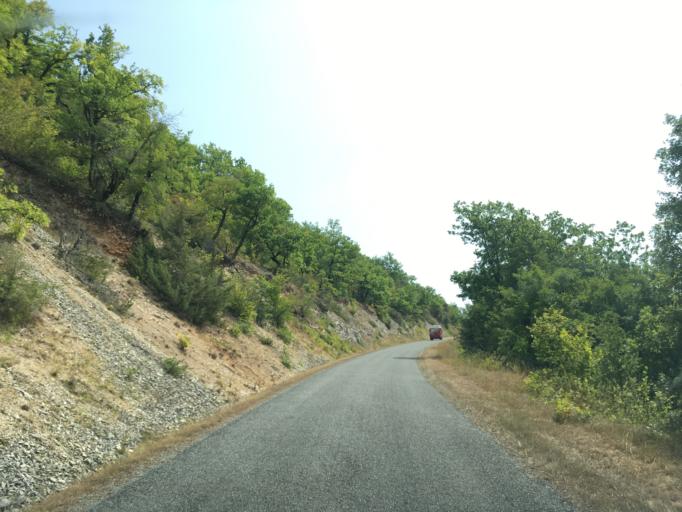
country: FR
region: Midi-Pyrenees
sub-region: Departement du Lot
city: Gramat
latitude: 44.7630
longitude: 1.5877
